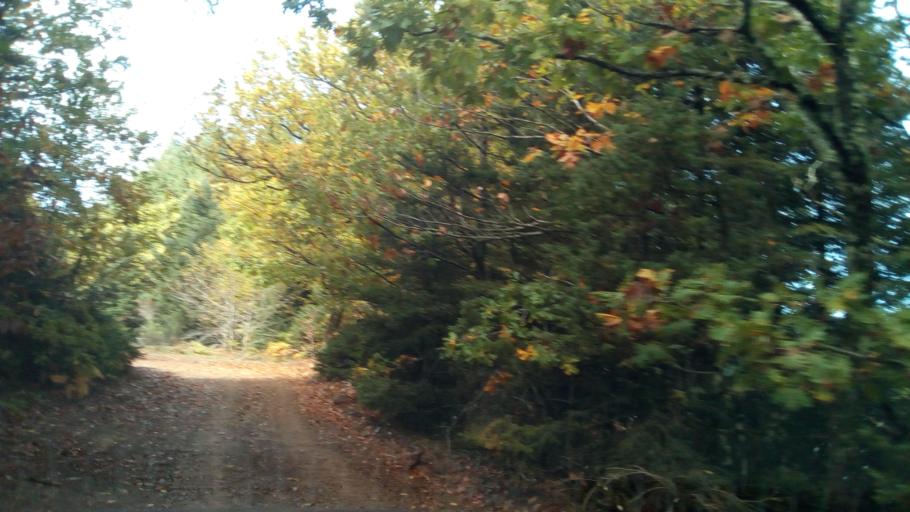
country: GR
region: Central Greece
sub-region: Nomos Fokidos
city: Lidoriki
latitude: 38.4818
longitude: 22.0544
